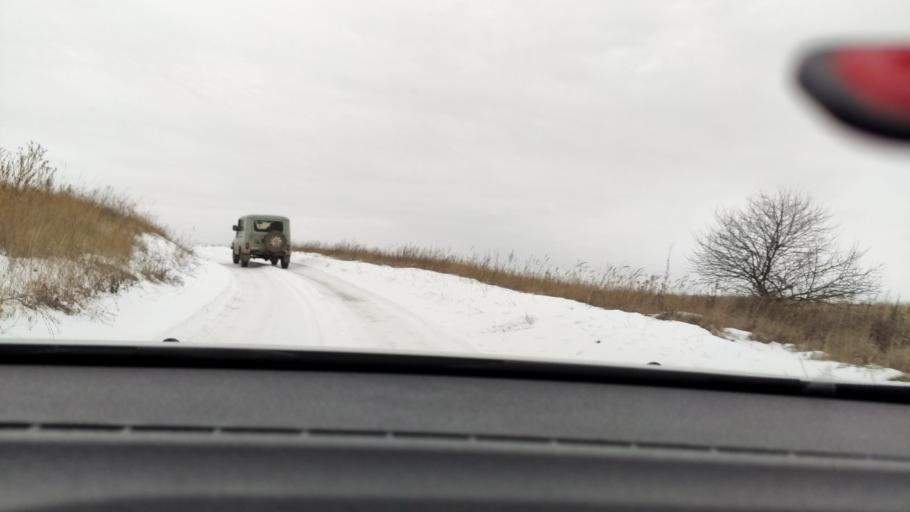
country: RU
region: Voronezj
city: Semiluki
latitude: 51.7111
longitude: 38.9794
